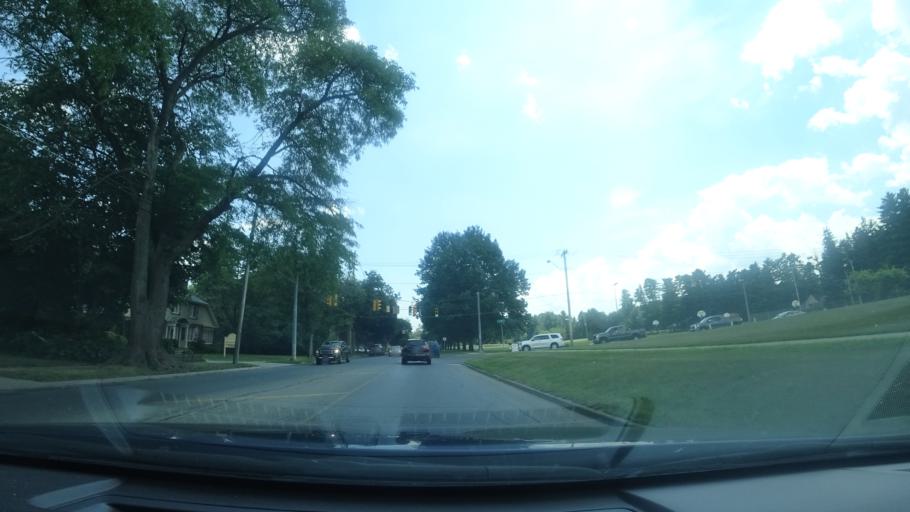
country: US
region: New York
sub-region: Warren County
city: Glens Falls
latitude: 43.3230
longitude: -73.6614
